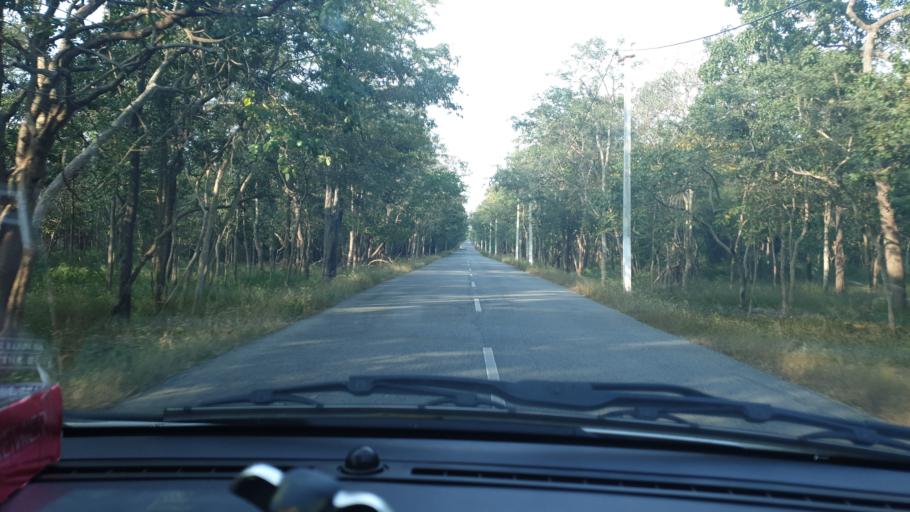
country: IN
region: Andhra Pradesh
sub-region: Kurnool
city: Srisailam
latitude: 16.2957
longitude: 78.7310
